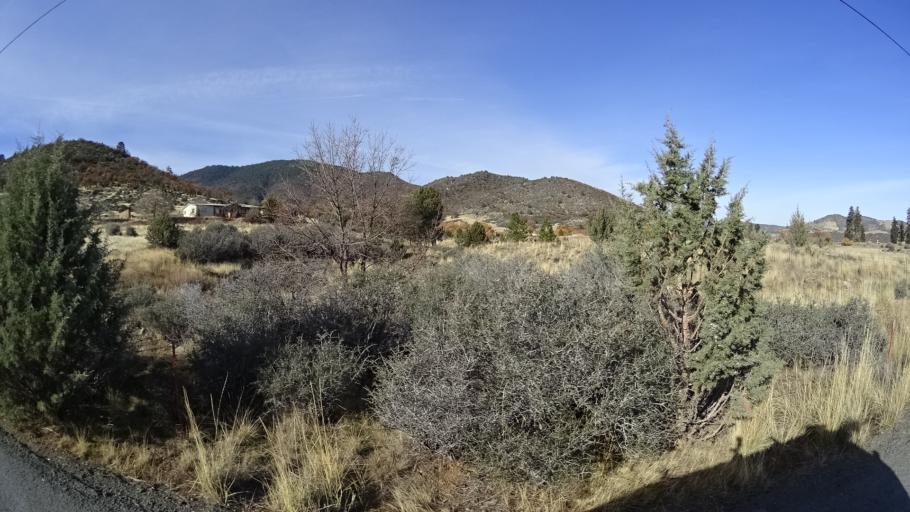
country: US
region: California
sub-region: Siskiyou County
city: Montague
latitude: 41.6332
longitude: -122.5700
